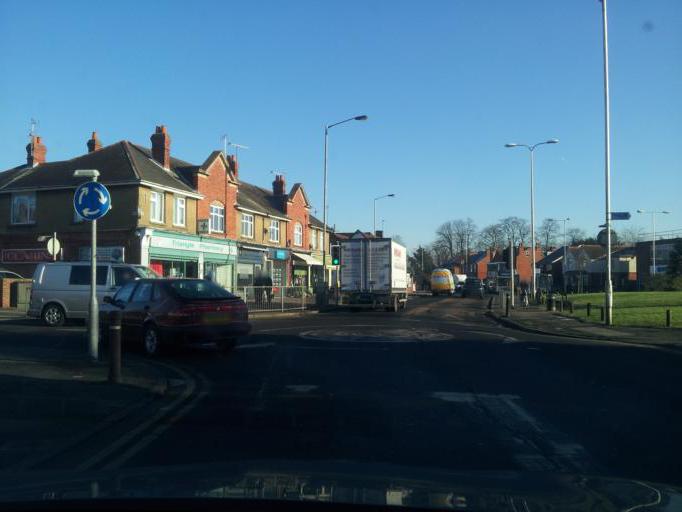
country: GB
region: England
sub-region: West Berkshire
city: Tilehurst
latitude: 51.4580
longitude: -1.0415
